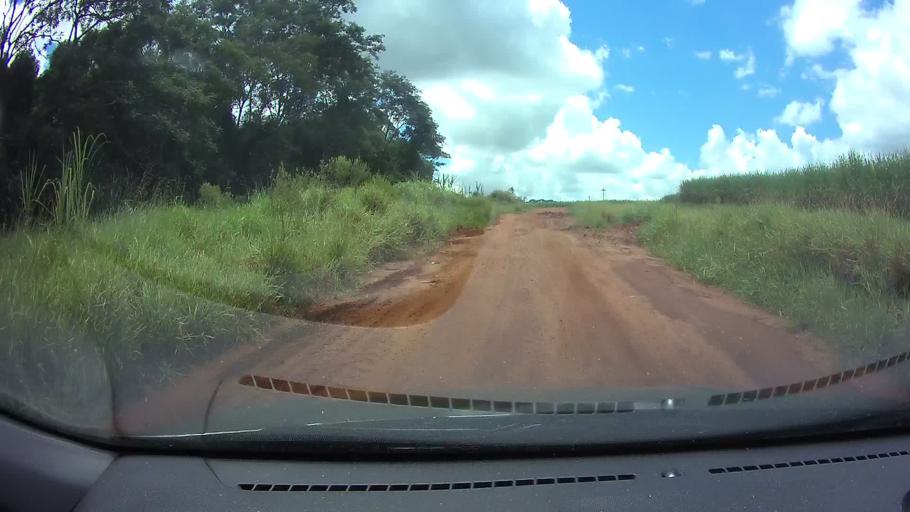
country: PY
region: Paraguari
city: La Colmena
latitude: -25.9523
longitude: -56.7678
